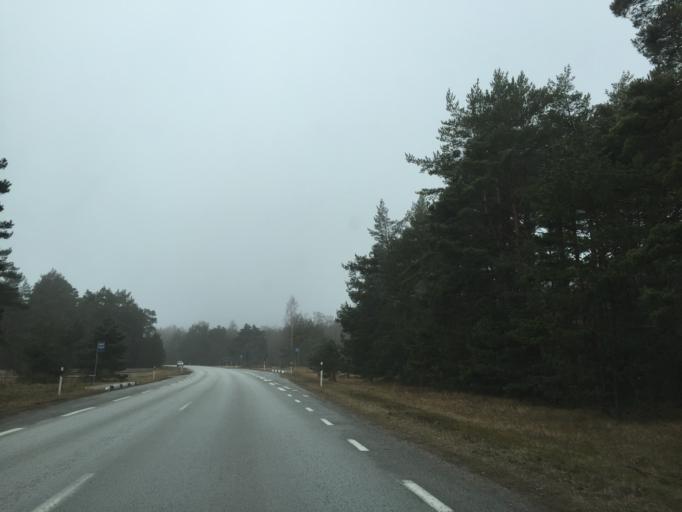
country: EE
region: Saare
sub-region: Kuressaare linn
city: Kuressaare
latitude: 58.1929
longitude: 22.2711
